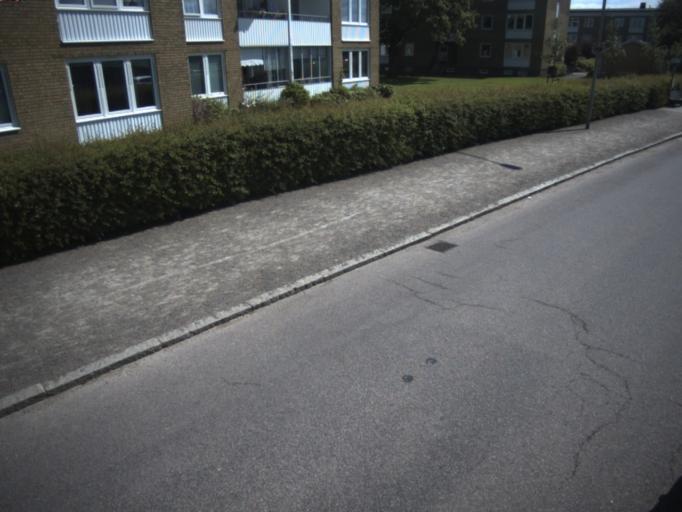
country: SE
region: Skane
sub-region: Helsingborg
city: Helsingborg
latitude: 56.0723
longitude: 12.7052
